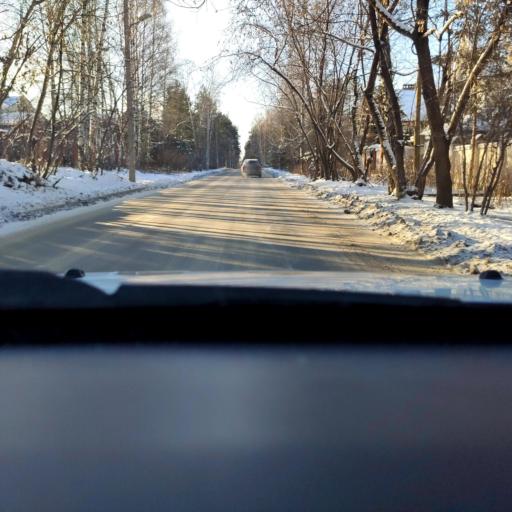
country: RU
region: Perm
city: Perm
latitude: 58.0536
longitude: 56.2955
